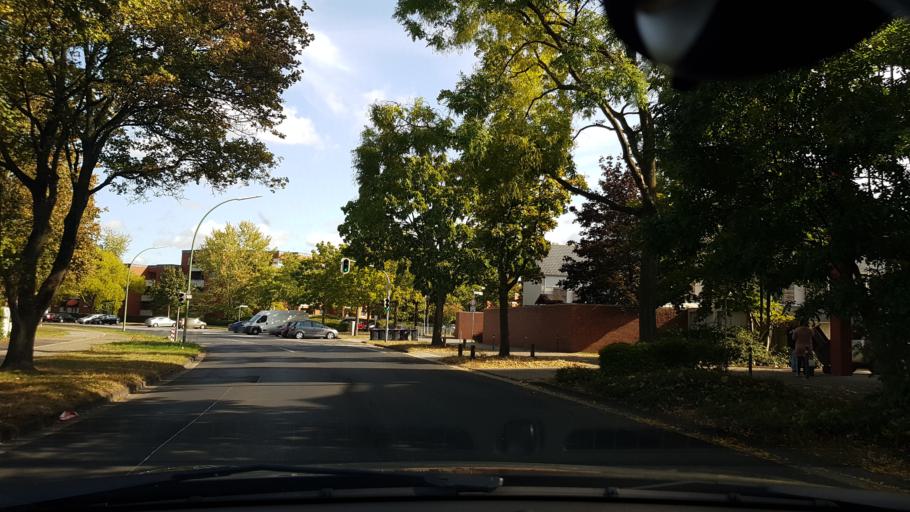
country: DE
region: North Rhine-Westphalia
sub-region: Regierungsbezirk Dusseldorf
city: Neuss
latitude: 51.1535
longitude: 6.7030
